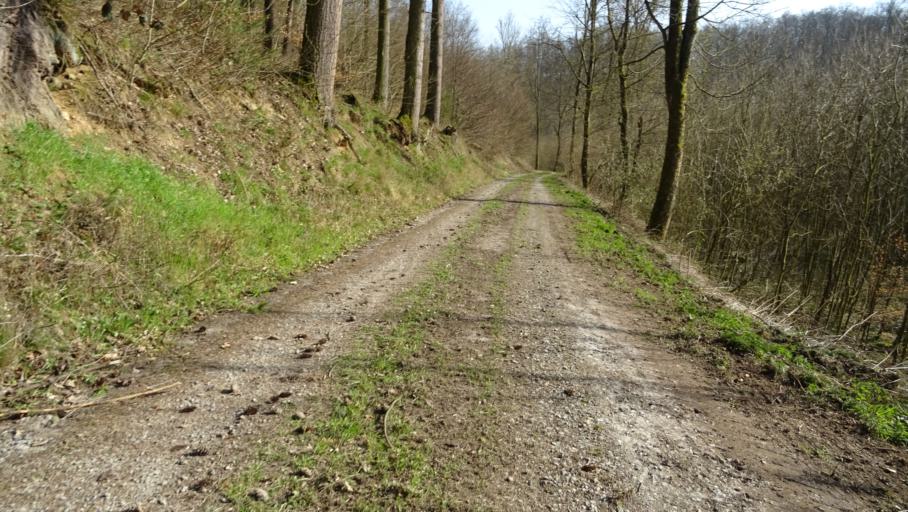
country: DE
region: Baden-Wuerttemberg
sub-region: Regierungsbezirk Stuttgart
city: Roigheim
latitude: 49.3811
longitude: 9.3476
